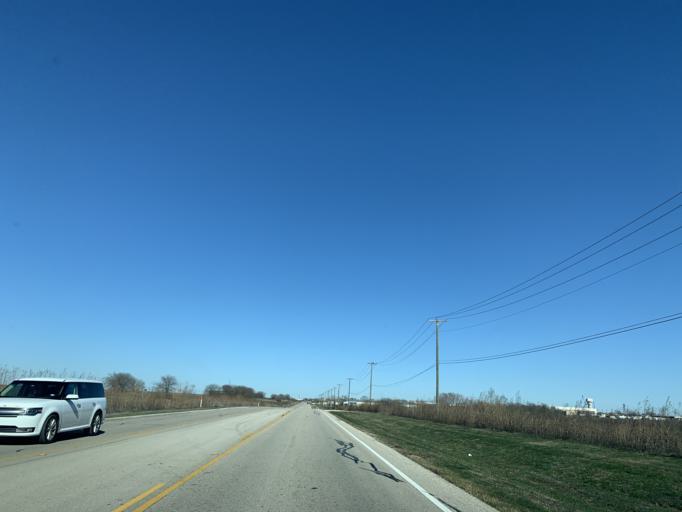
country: US
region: Texas
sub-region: Williamson County
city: Hutto
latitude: 30.5416
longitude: -97.5739
